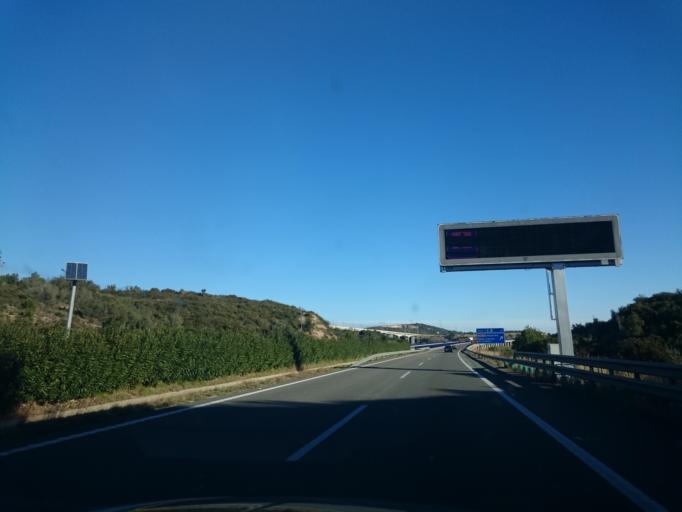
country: ES
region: Catalonia
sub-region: Provincia de Tarragona
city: Amposta
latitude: 40.7230
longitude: 0.5659
